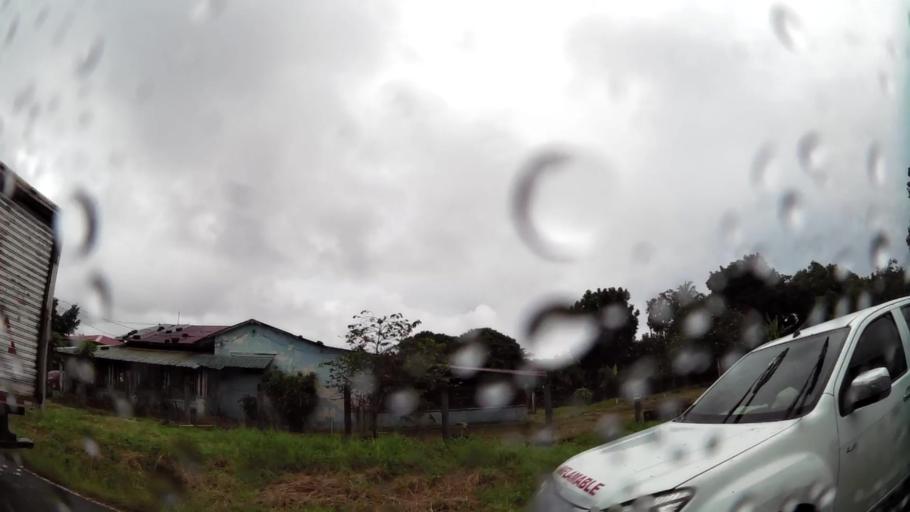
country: PA
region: Chiriqui
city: David
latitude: 8.4334
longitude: -82.4399
